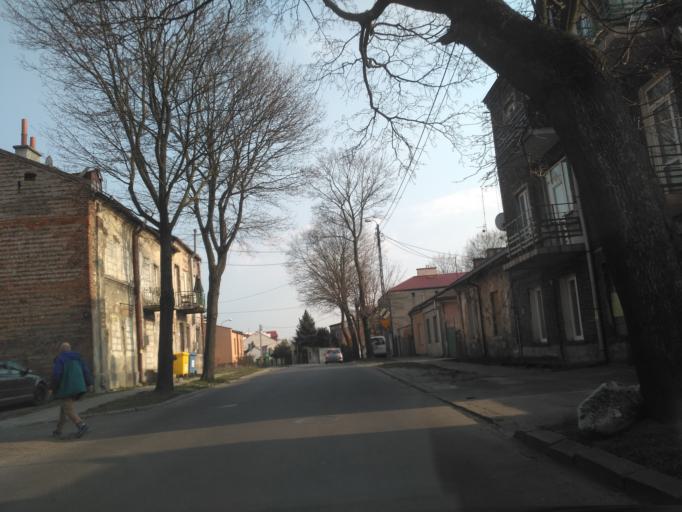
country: PL
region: Lublin Voivodeship
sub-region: Powiat lubelski
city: Lublin
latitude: 51.2294
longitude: 22.5803
